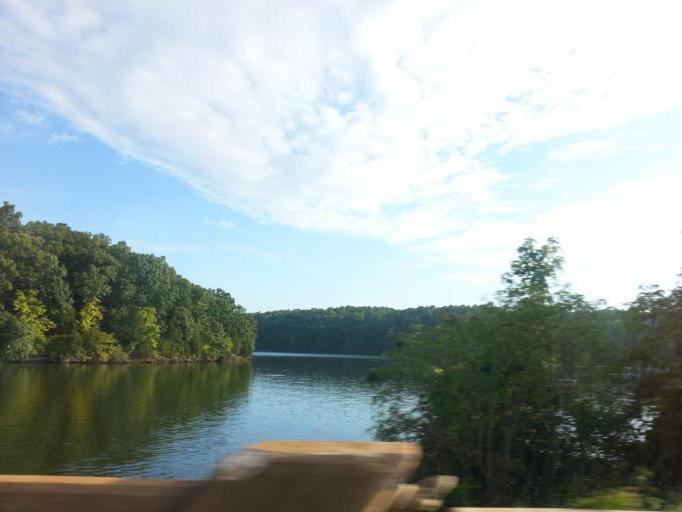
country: US
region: Alabama
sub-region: Lauderdale County
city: Rogersville
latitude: 34.8433
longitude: -87.3708
